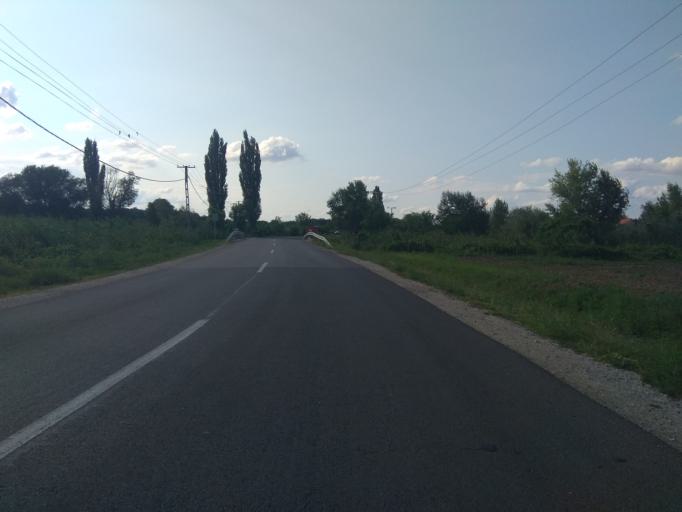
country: HU
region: Borsod-Abauj-Zemplen
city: Mezocsat
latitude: 47.8389
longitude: 20.9001
